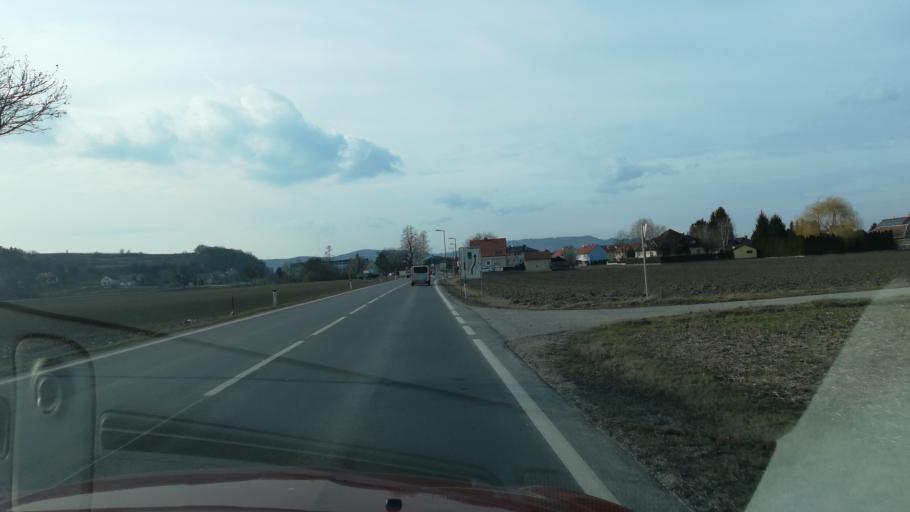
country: AT
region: Lower Austria
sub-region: Politischer Bezirk Sankt Polten
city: Traismauer
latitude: 48.3482
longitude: 15.7613
